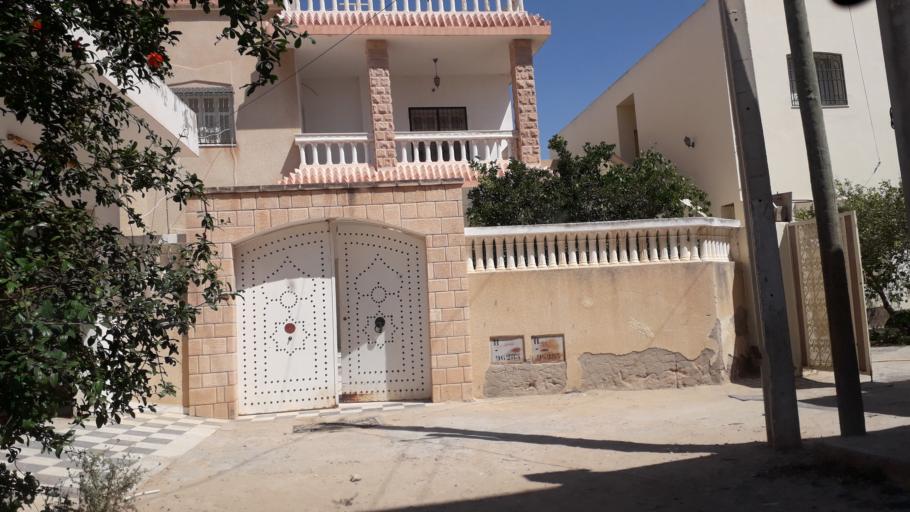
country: TN
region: Safaqis
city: Al Qarmadah
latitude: 34.8197
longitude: 10.7639
